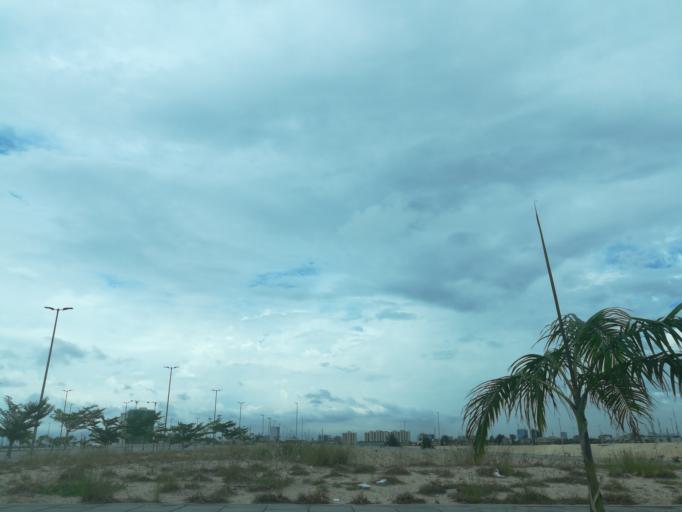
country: NG
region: Lagos
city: Ikoyi
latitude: 6.4117
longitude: 3.4174
